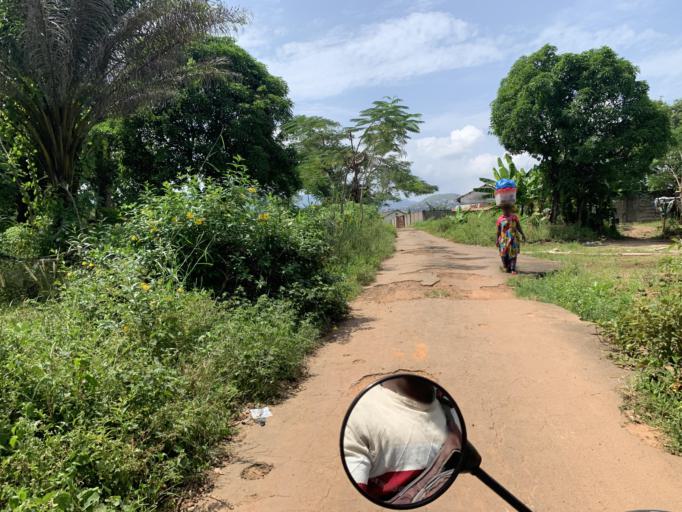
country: SL
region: Western Area
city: Hastings
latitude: 8.4125
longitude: -13.1294
